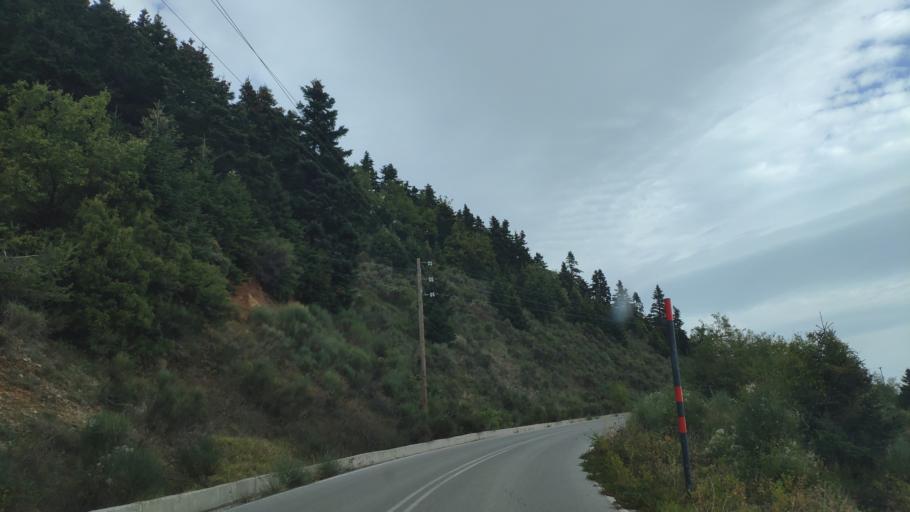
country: GR
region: Central Greece
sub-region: Nomos Fokidos
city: Amfissa
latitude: 38.6877
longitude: 22.3188
